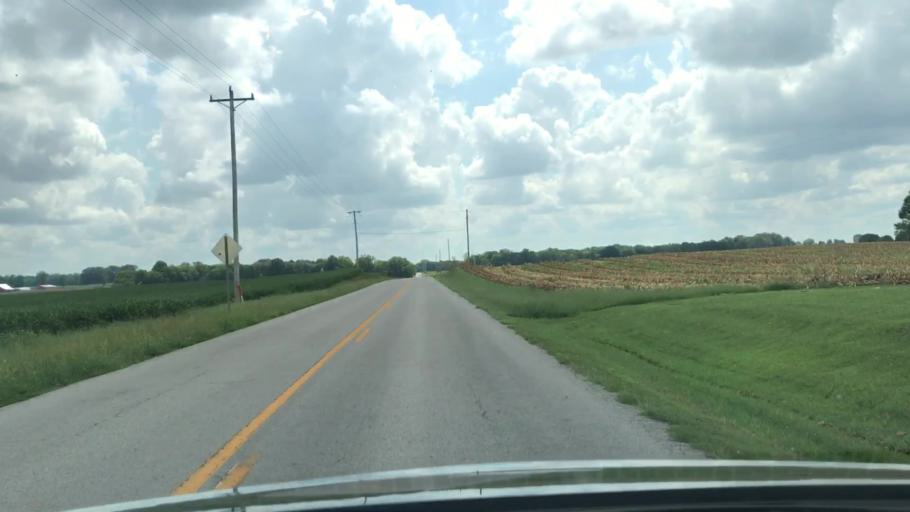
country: US
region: Kentucky
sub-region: Todd County
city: Elkton
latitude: 36.7703
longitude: -87.1154
